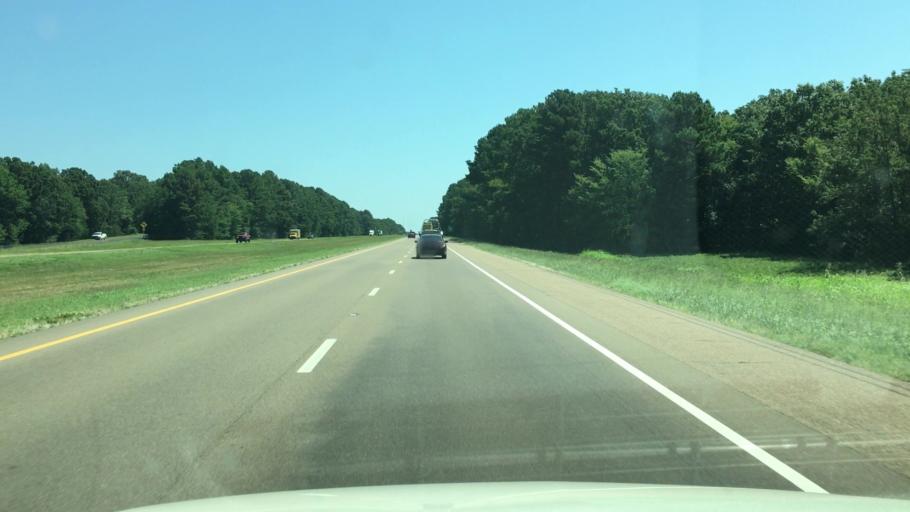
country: US
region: Texas
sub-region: Bowie County
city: New Boston
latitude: 33.4536
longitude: -94.4952
